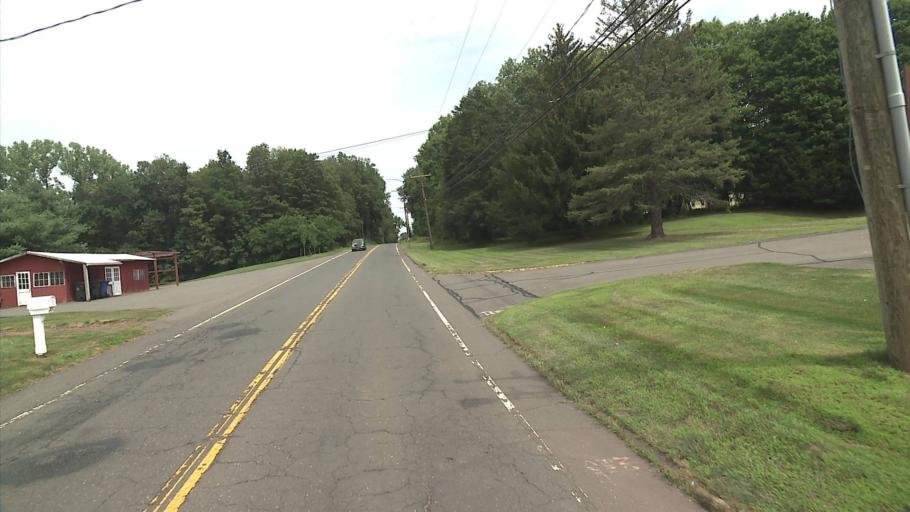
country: US
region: Connecticut
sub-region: Hartford County
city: Kensington
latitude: 41.6070
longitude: -72.7959
